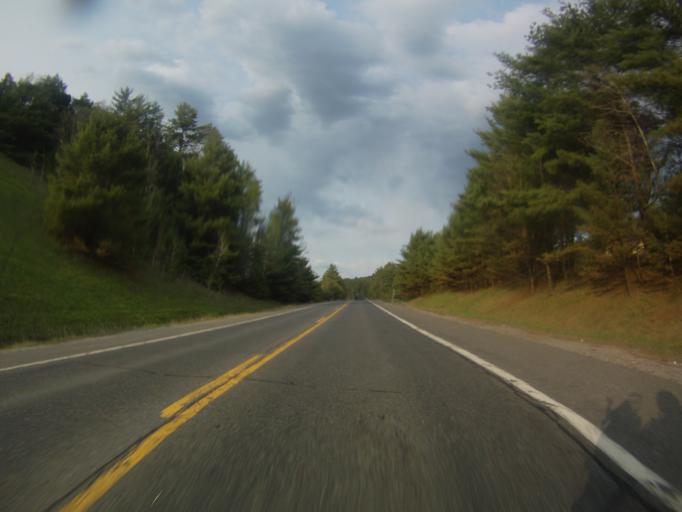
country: US
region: New York
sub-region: Warren County
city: Warrensburg
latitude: 43.6596
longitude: -73.7920
